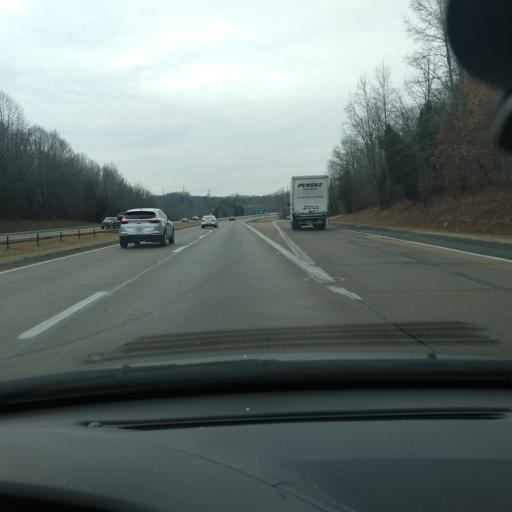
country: US
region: North Carolina
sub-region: Davidson County
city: Midway
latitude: 36.0193
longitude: -80.2366
